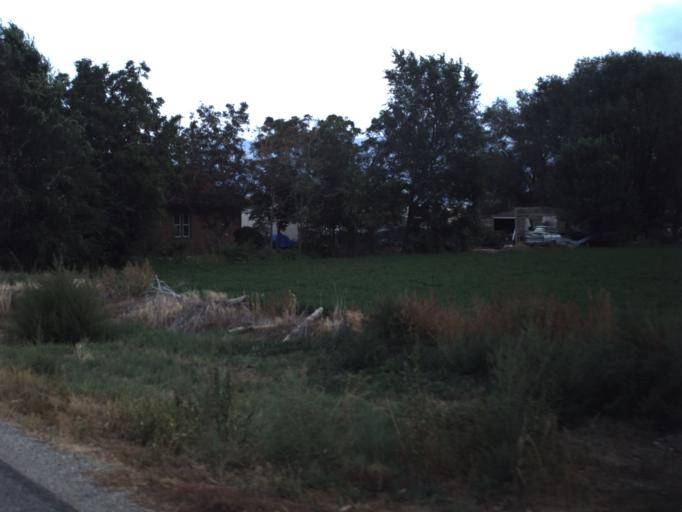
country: US
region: Utah
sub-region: Weber County
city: Plain City
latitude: 41.2653
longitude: -112.0924
